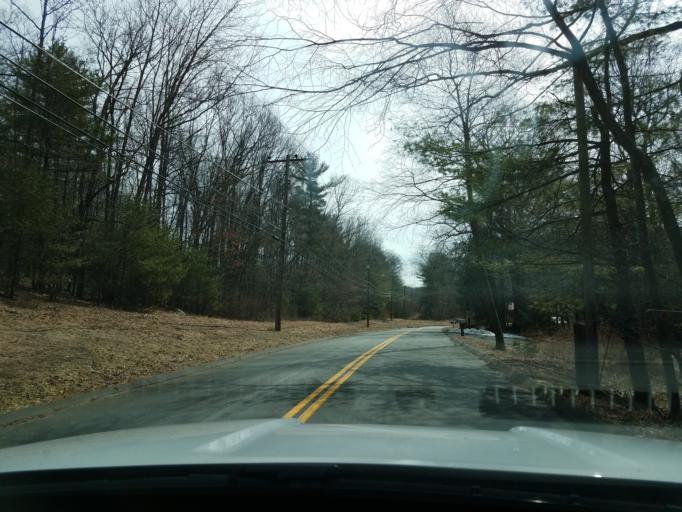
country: US
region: Connecticut
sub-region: Hartford County
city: Collinsville
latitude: 41.7802
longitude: -72.9162
